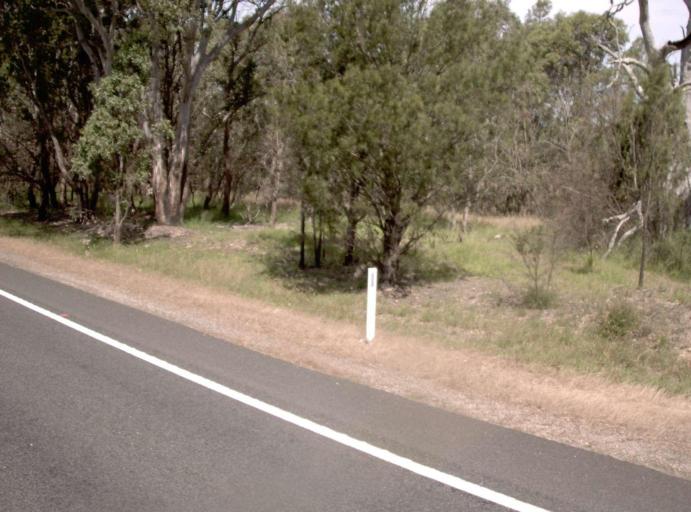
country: AU
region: Victoria
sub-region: East Gippsland
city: Bairnsdale
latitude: -37.8642
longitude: 147.4987
